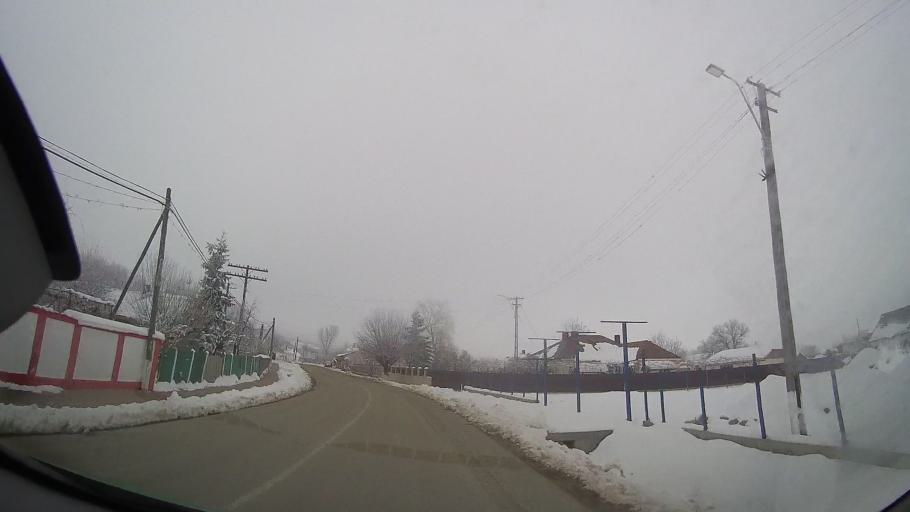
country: RO
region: Iasi
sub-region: Comuna Dagata
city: Dagata
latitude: 46.9178
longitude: 27.2024
